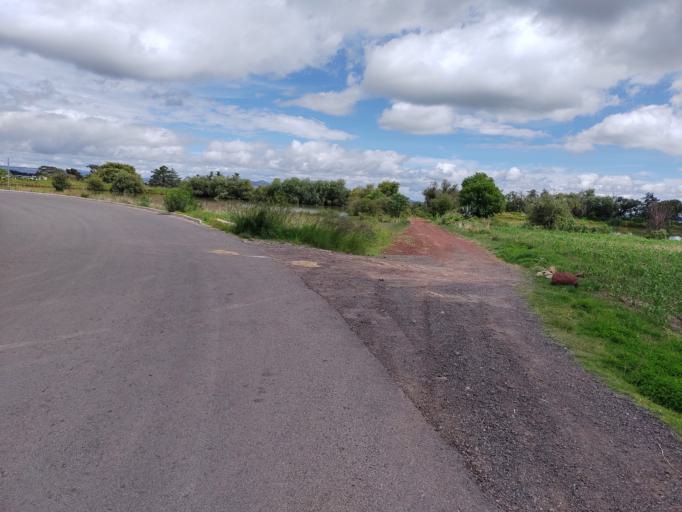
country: MX
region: Mexico
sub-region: Aculco
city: Gunyo Poniente (San Jose Gunyo)
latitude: 20.1187
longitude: -99.8782
